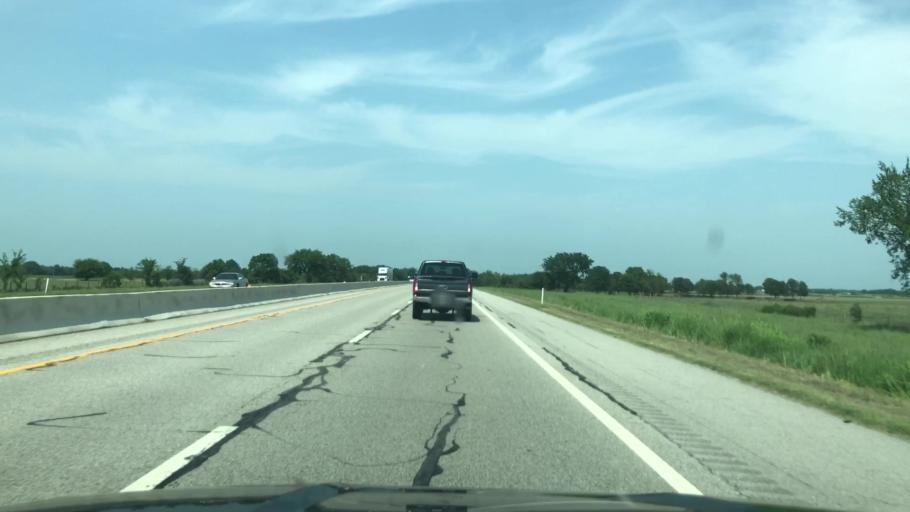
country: US
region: Oklahoma
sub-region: Ottawa County
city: Fairland
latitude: 36.7507
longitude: -94.9037
